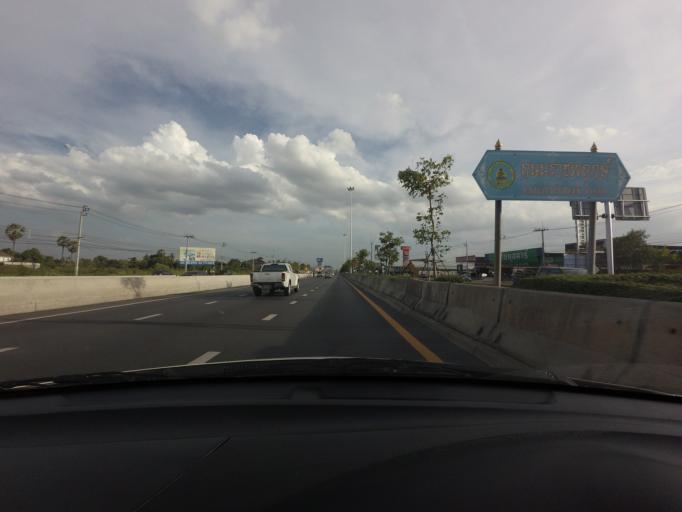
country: TH
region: Nonthaburi
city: Bang Bua Thong
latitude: 13.9239
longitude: 100.4527
